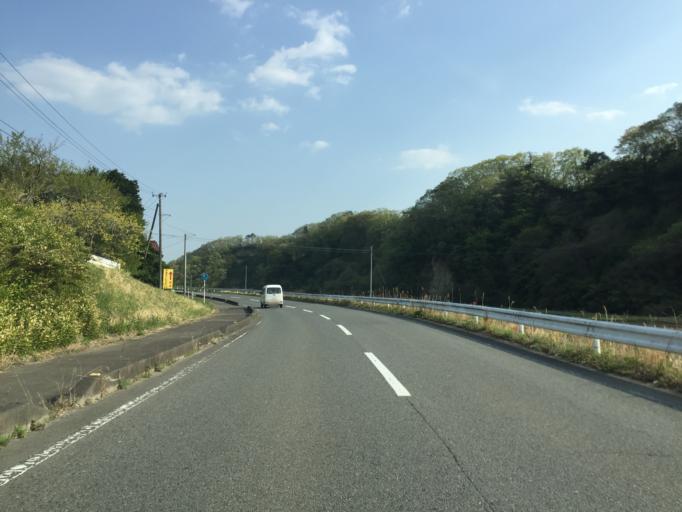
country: JP
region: Fukushima
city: Iwaki
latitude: 36.9956
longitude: 140.7905
